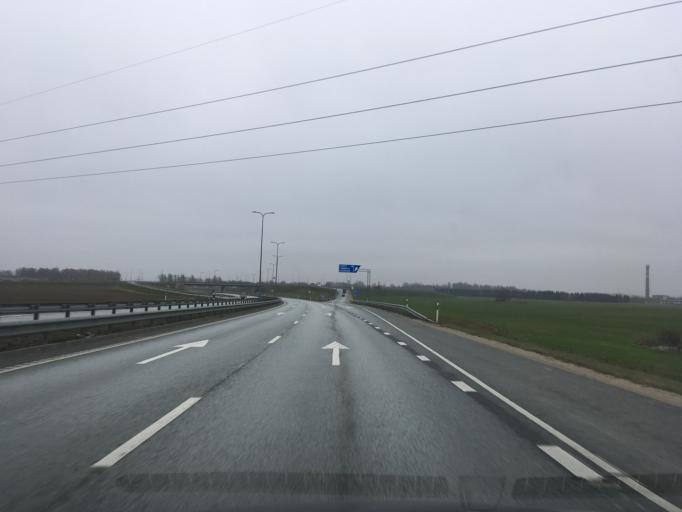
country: EE
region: Ida-Virumaa
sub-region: Kohtla-Jaerve linn
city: Kohtla-Jarve
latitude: 59.3892
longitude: 27.3408
